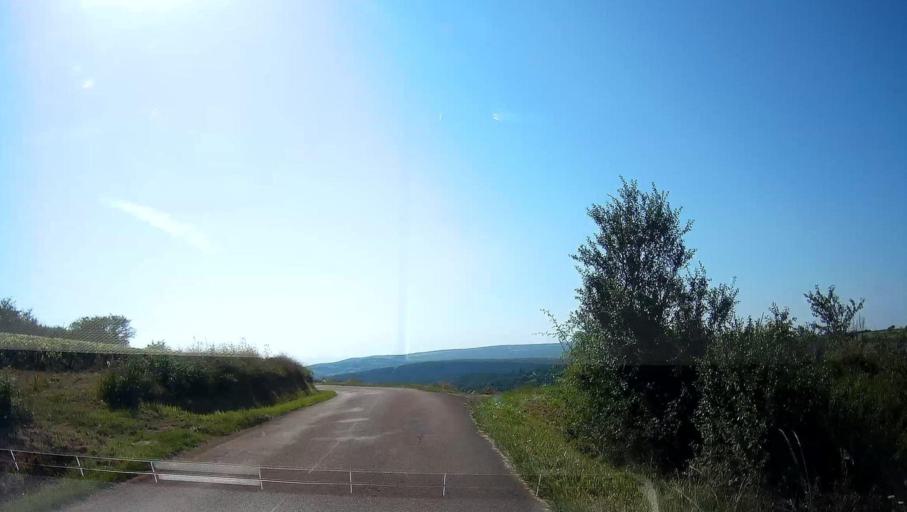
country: FR
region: Bourgogne
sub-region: Departement de Saone-et-Loire
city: Couches
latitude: 46.8897
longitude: 4.5858
